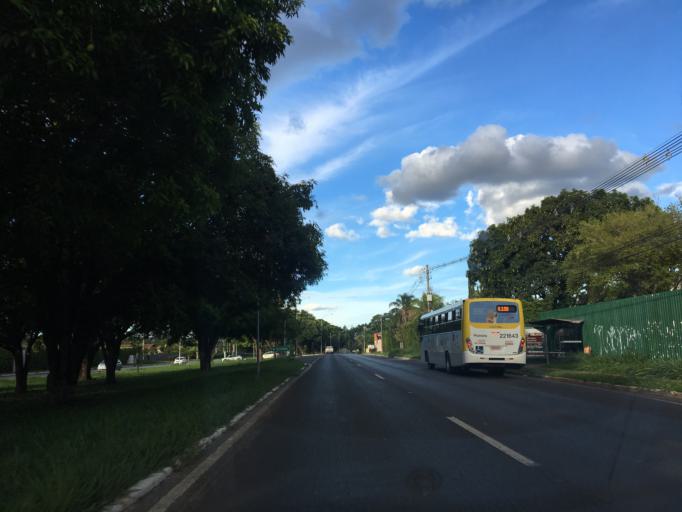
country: BR
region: Federal District
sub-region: Brasilia
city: Brasilia
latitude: -15.8534
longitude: -47.9130
